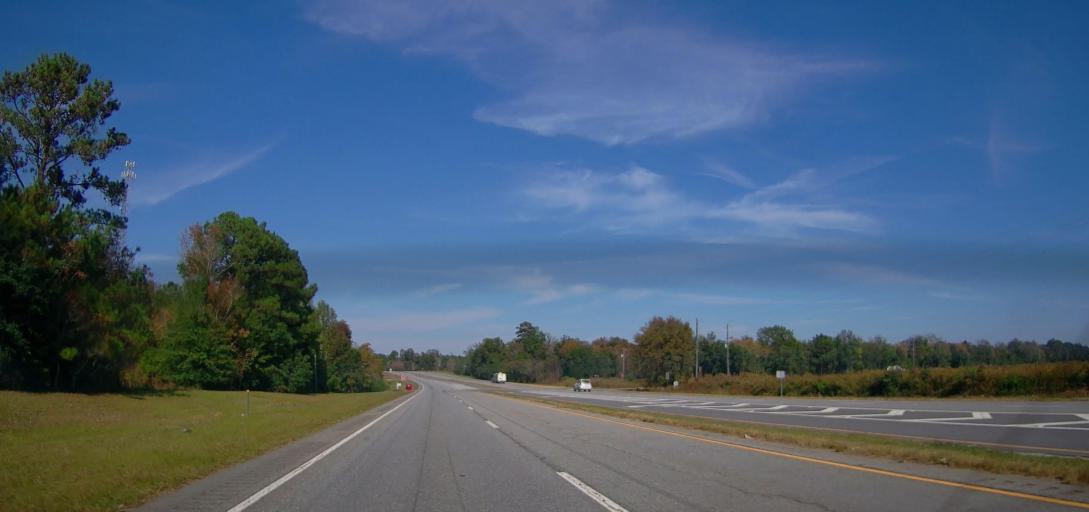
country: US
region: Georgia
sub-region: Dougherty County
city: Albany
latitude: 31.6572
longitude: -83.9995
